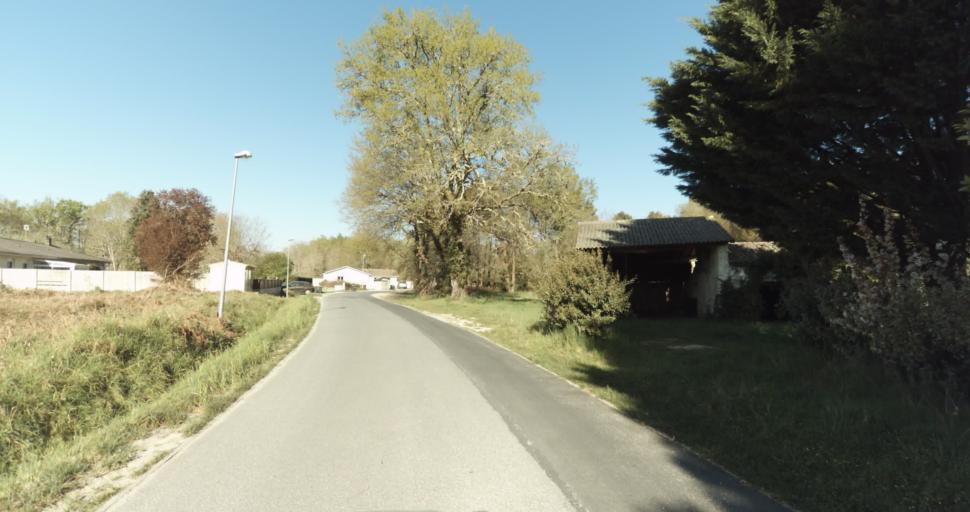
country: FR
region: Aquitaine
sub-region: Departement de la Gironde
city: Martignas-sur-Jalle
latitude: 44.8043
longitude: -0.8420
